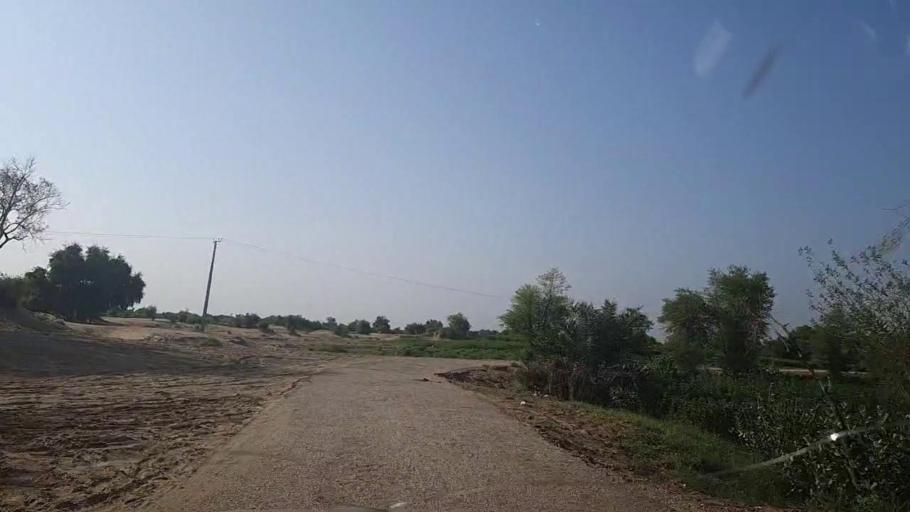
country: PK
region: Sindh
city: Khanpur
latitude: 27.7258
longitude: 69.3309
